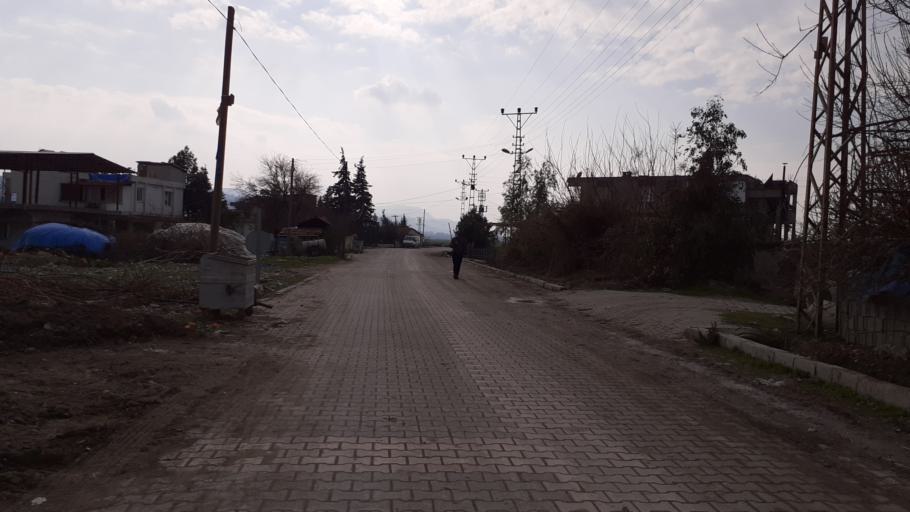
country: TR
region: Hatay
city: Kastal
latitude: 36.2628
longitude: 36.2439
